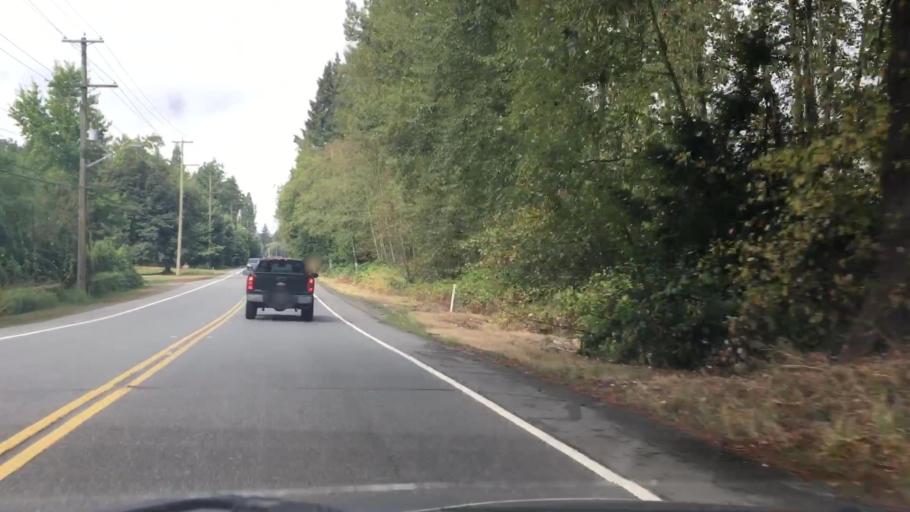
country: CA
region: British Columbia
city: Langley
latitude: 49.1040
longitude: -122.5739
